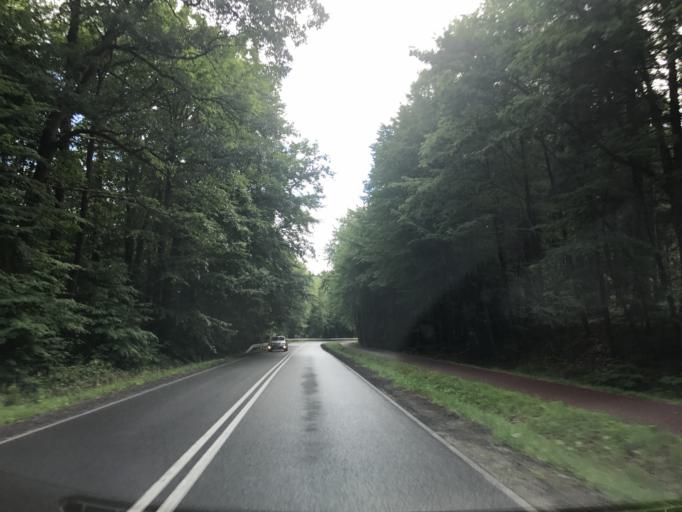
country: PL
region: West Pomeranian Voivodeship
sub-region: Powiat koszalinski
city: Sianow
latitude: 54.2077
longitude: 16.2368
